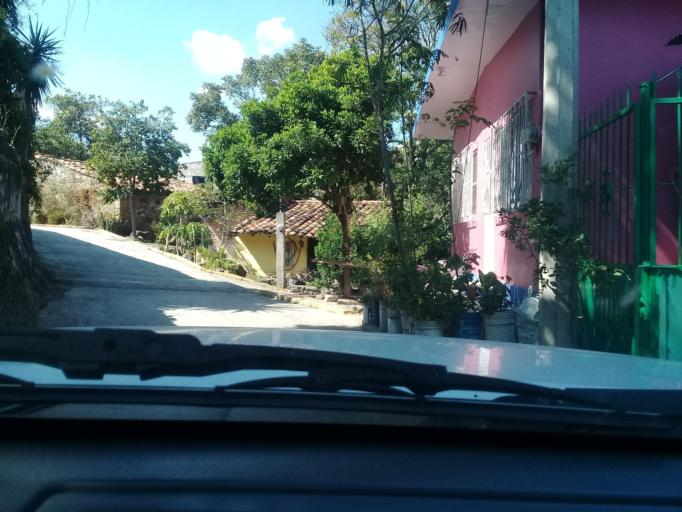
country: MX
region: Veracruz
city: Actopan
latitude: 19.4801
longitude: -96.6448
